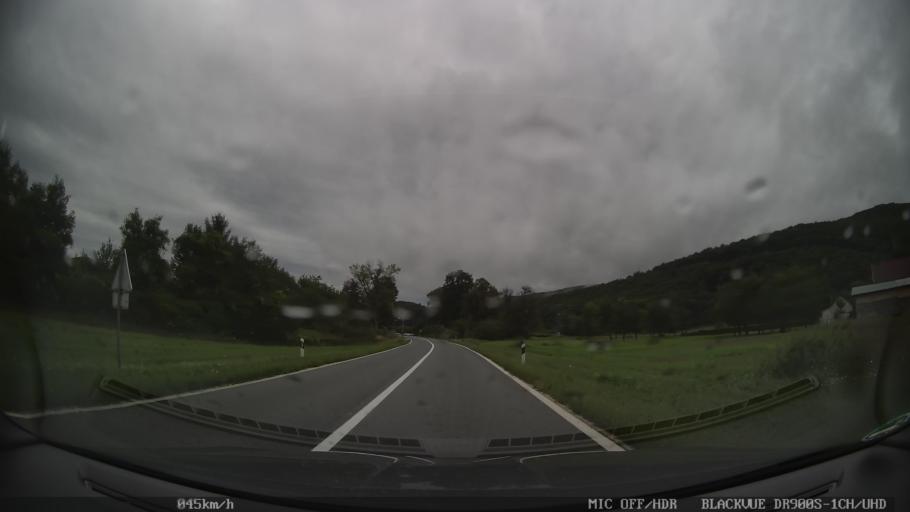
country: HR
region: Licko-Senjska
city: Brinje
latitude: 44.9405
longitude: 15.1258
